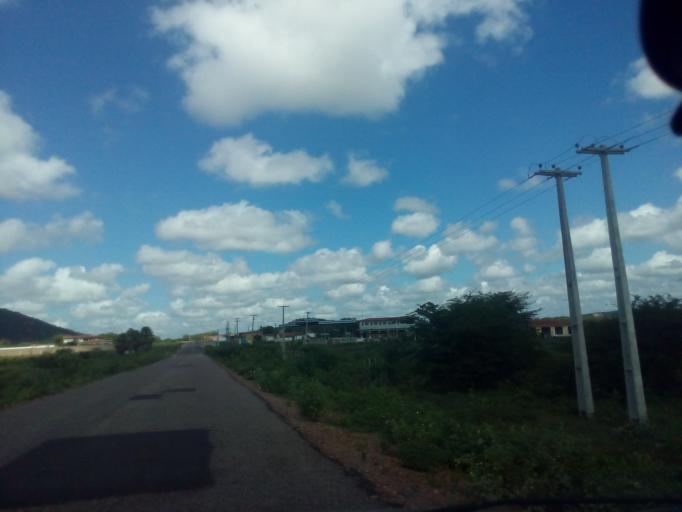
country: BR
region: Rio Grande do Norte
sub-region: Sao Tome
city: Sao Tome
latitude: -5.9695
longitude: -35.9246
